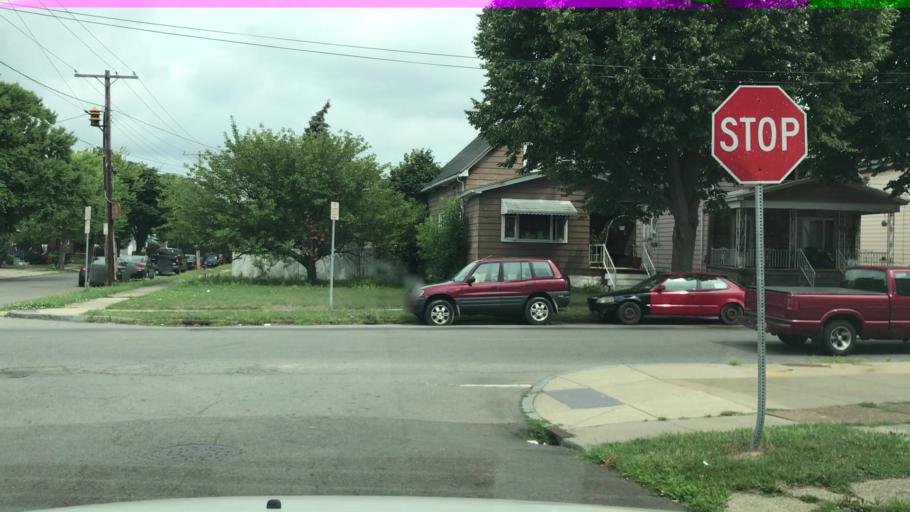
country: US
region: New York
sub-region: Erie County
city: Sloan
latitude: 42.9097
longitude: -78.8015
